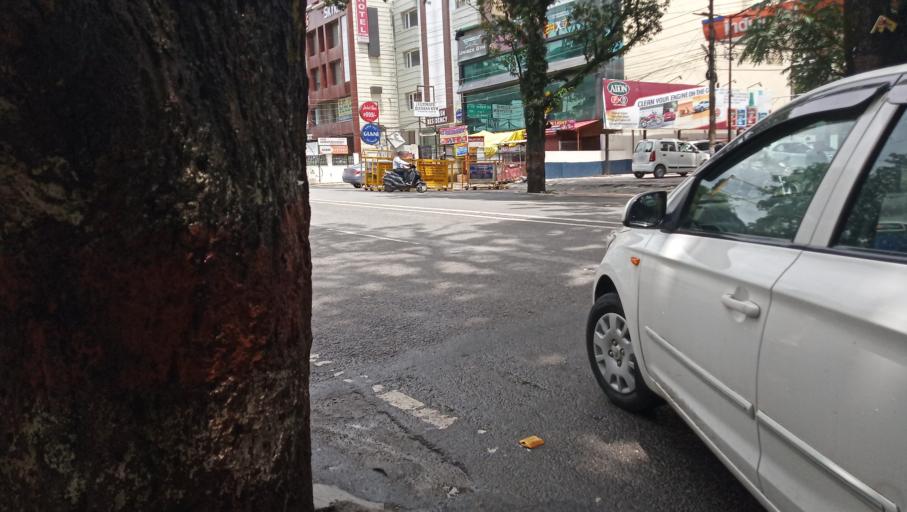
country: IN
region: Uttarakhand
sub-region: Dehradun
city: Dehradun
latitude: 30.3640
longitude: 78.0691
